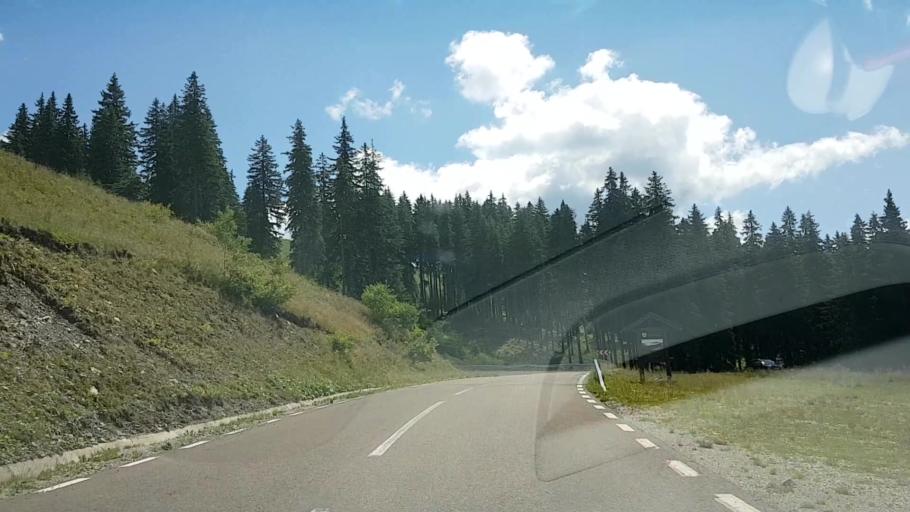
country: RO
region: Suceava
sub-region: Comuna Sadova
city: Sadova
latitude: 47.4584
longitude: 25.5286
